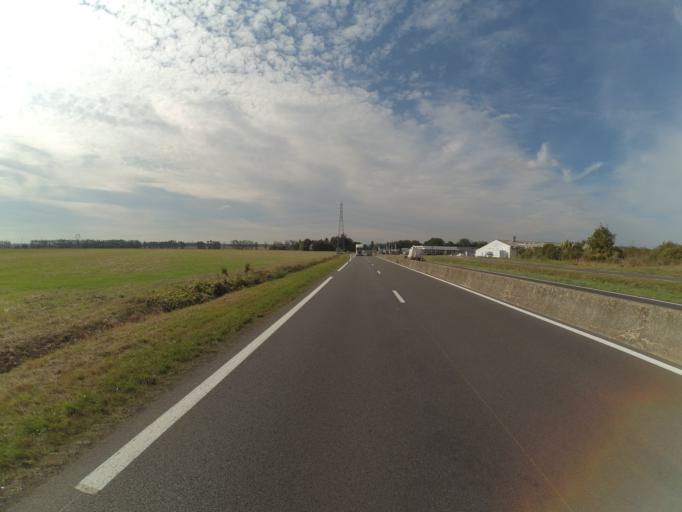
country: FR
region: Pays de la Loire
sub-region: Departement de Maine-et-Loire
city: Distre
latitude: 47.2296
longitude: -0.1289
